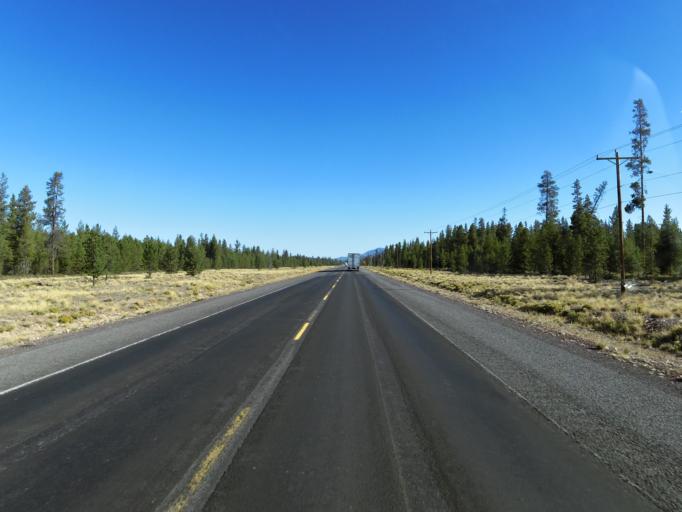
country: US
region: Oregon
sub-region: Deschutes County
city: La Pine
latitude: 43.1490
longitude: -121.7968
